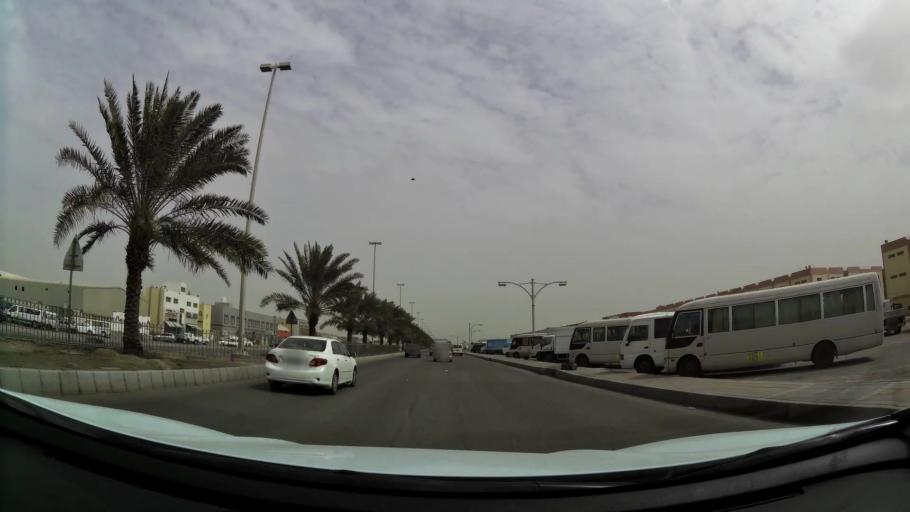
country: AE
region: Abu Dhabi
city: Abu Dhabi
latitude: 24.3451
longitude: 54.4879
